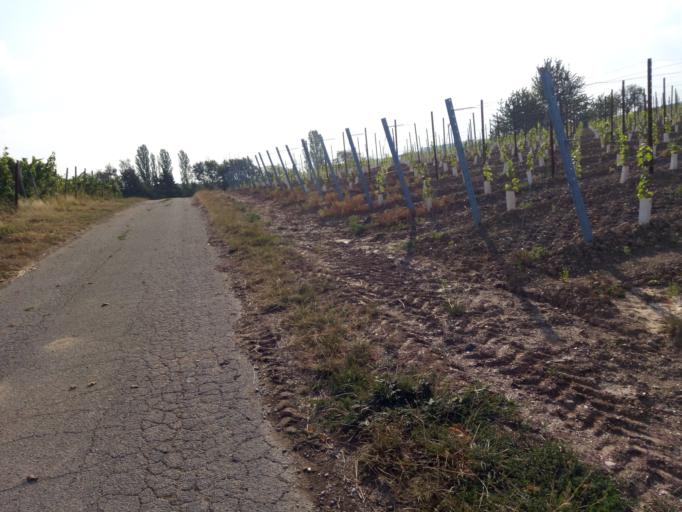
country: DE
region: Rheinland-Pfalz
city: Waldlaubersheim
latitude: 49.9257
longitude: 7.8360
